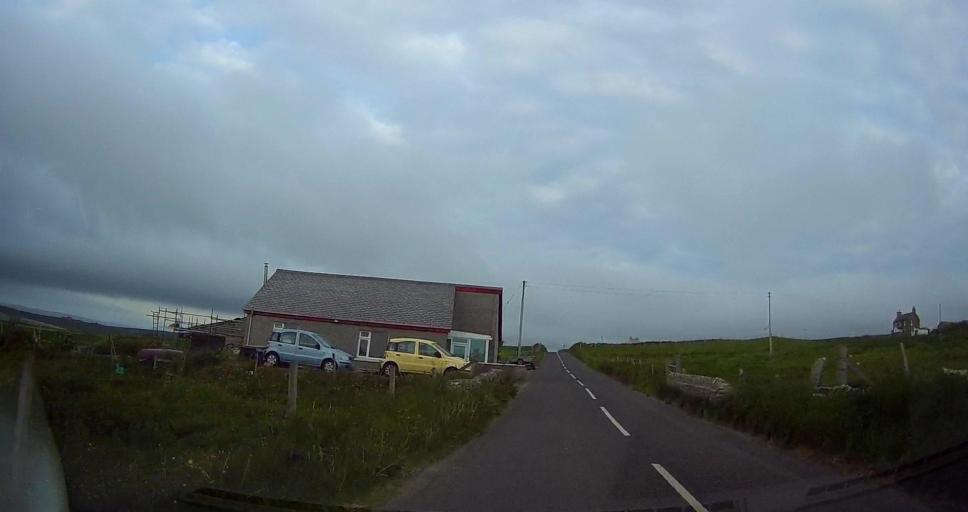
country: GB
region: Scotland
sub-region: Orkney Islands
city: Orkney
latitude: 59.1190
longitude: -3.1203
